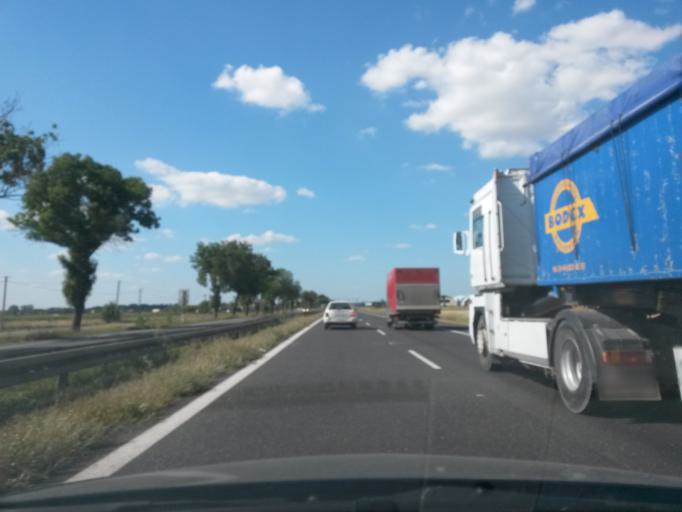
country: PL
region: Masovian Voivodeship
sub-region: Powiat nowodworski
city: Zakroczym
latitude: 52.4658
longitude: 20.5723
